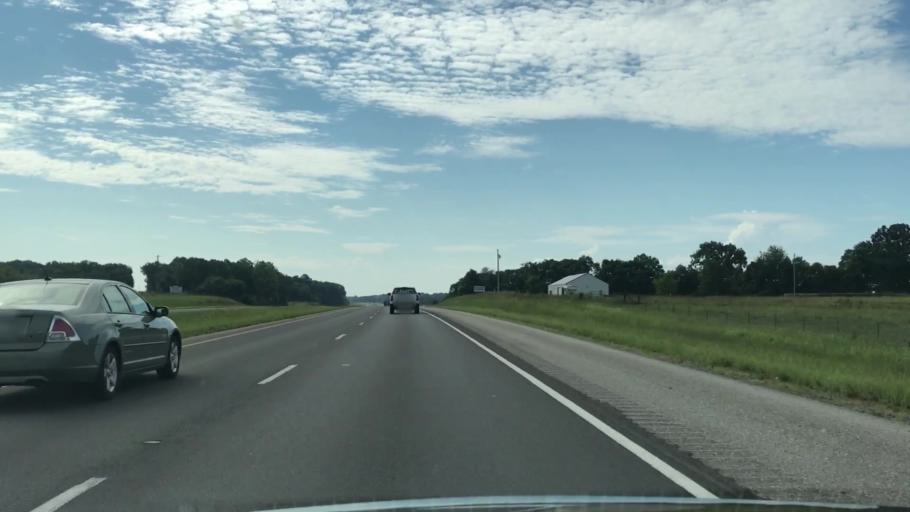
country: US
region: Kentucky
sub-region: Warren County
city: Plano
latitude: 36.8212
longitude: -86.3094
